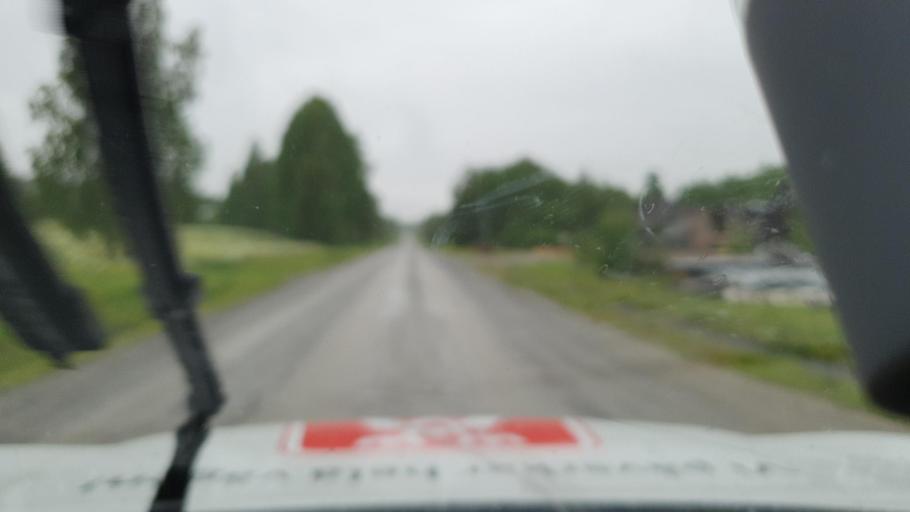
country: SE
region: Vaesterbotten
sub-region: Bjurholms Kommun
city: Bjurholm
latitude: 63.8655
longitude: 19.4642
